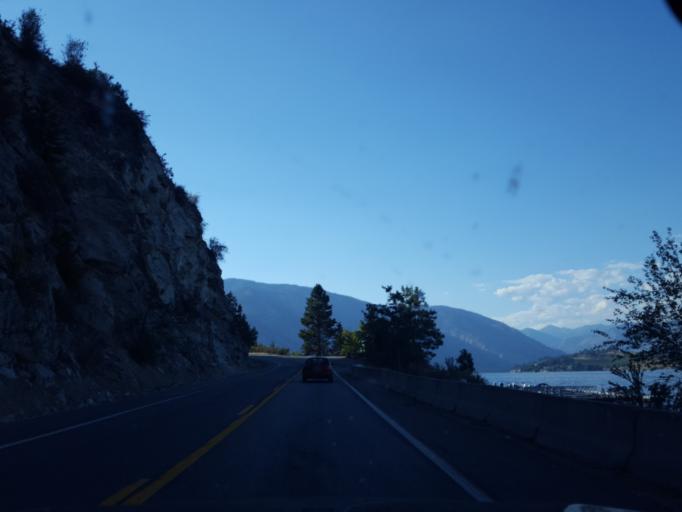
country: US
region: Washington
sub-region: Chelan County
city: Manson
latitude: 47.8648
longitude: -120.1747
